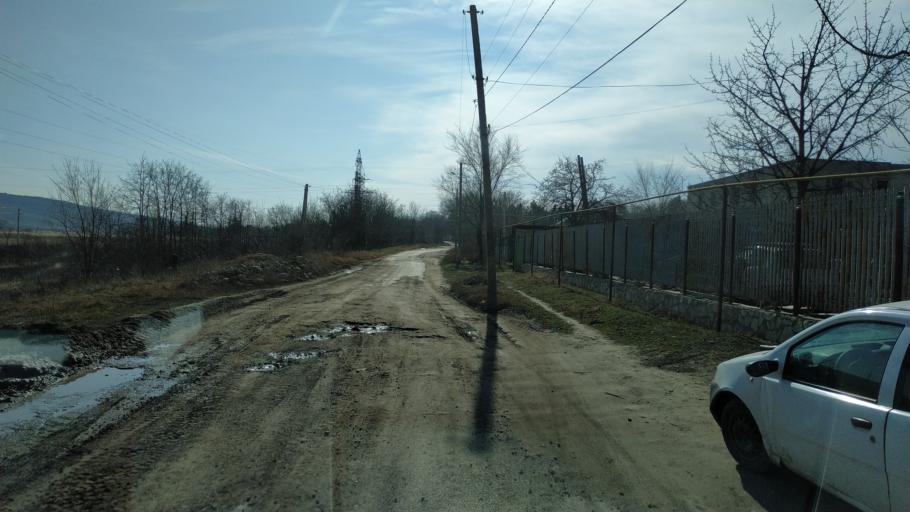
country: MD
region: Nisporeni
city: Nisporeni
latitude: 47.0623
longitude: 28.1717
